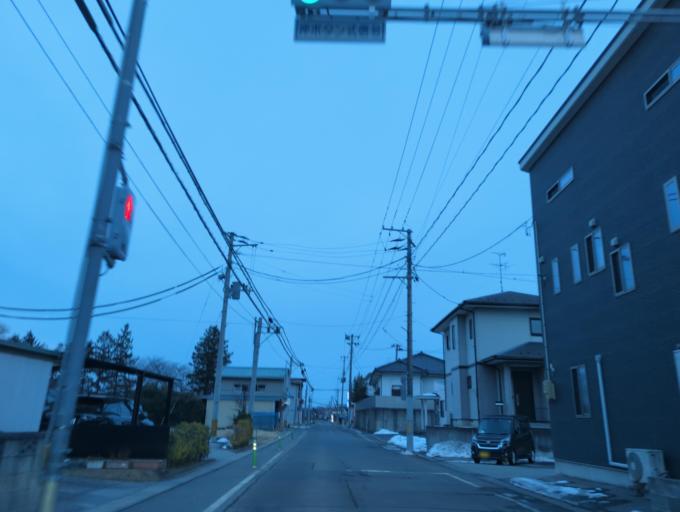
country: JP
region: Fukushima
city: Koriyama
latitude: 37.4286
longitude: 140.3852
